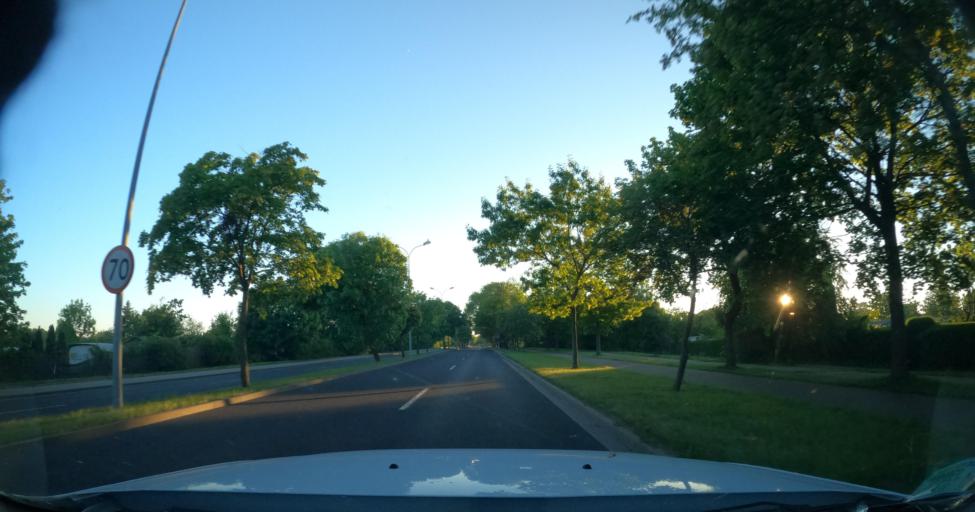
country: PL
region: Pomeranian Voivodeship
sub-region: Slupsk
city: Slupsk
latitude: 54.4697
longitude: 17.0686
